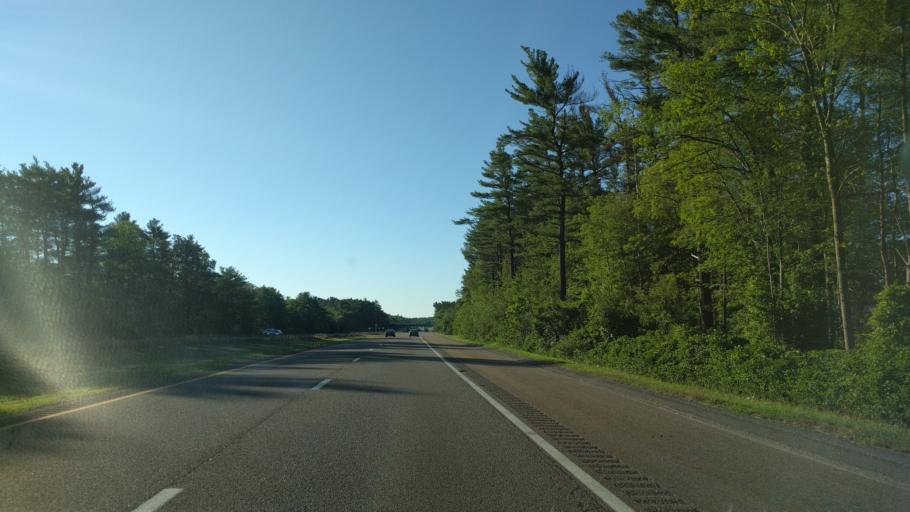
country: US
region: Massachusetts
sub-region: Plymouth County
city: Middleborough Center
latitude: 41.9068
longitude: -70.9716
